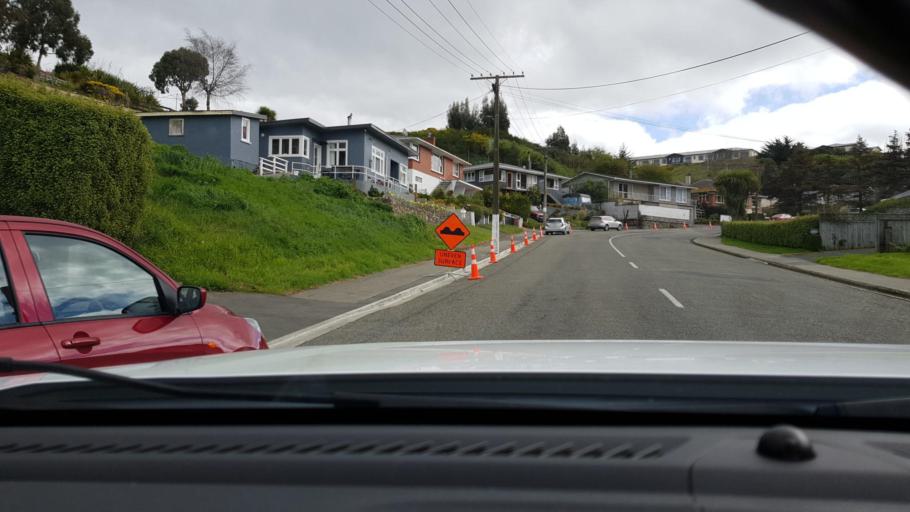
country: NZ
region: Otago
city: Oamaru
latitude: -45.0941
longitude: 170.9617
